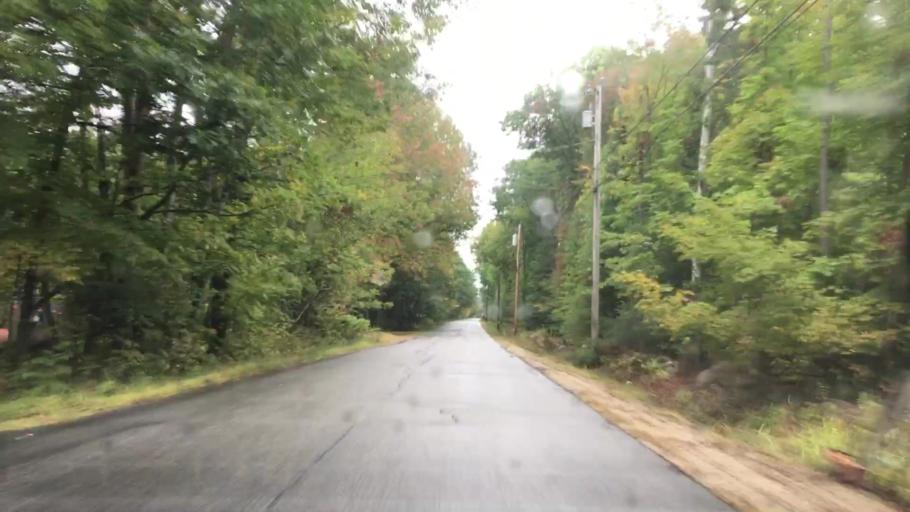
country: US
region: Maine
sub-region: Cumberland County
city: Harrison
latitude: 44.0671
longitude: -70.6306
